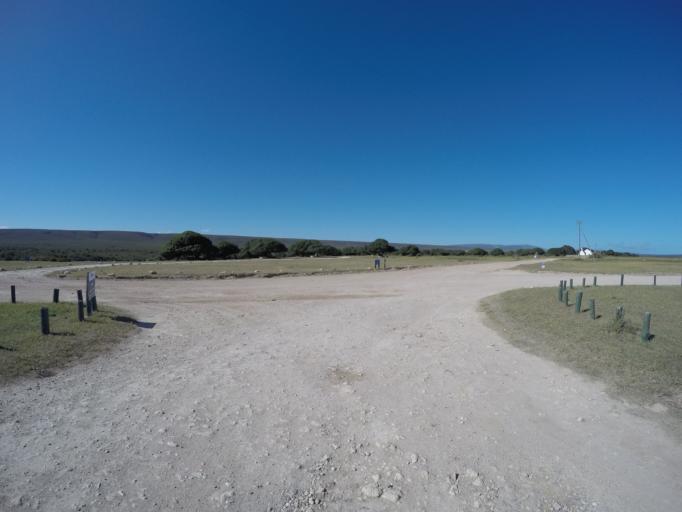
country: ZA
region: Western Cape
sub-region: Overberg District Municipality
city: Bredasdorp
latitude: -34.4539
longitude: 20.3997
